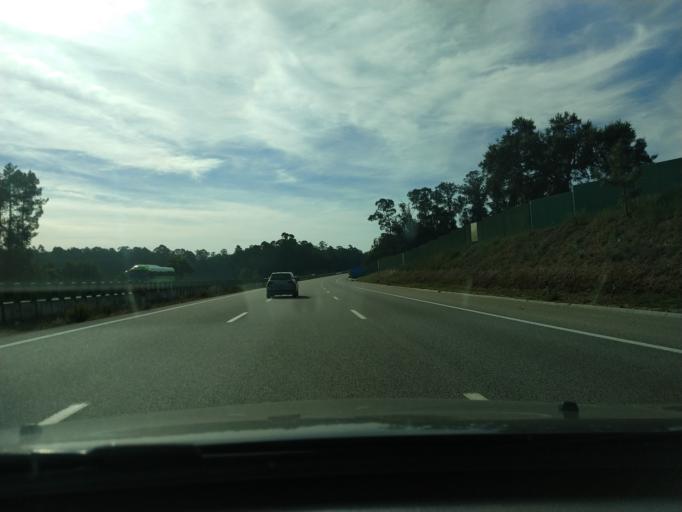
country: PT
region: Aveiro
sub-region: Ovar
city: Valega
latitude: 40.8435
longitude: -8.5564
